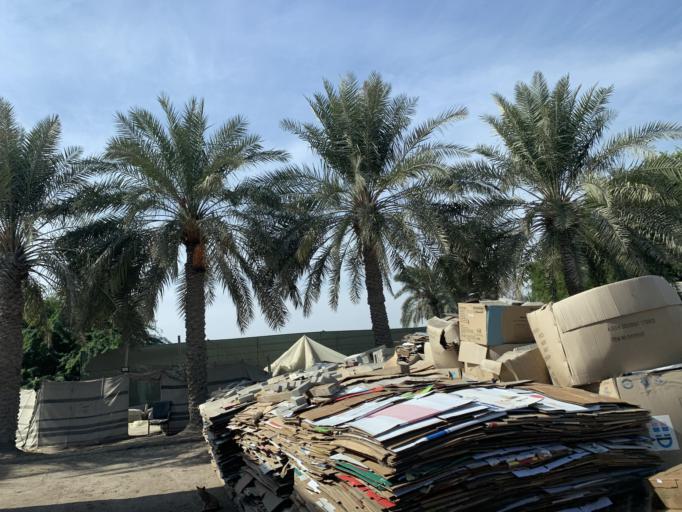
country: BH
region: Central Governorate
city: Madinat Hamad
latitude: 26.1269
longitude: 50.4724
